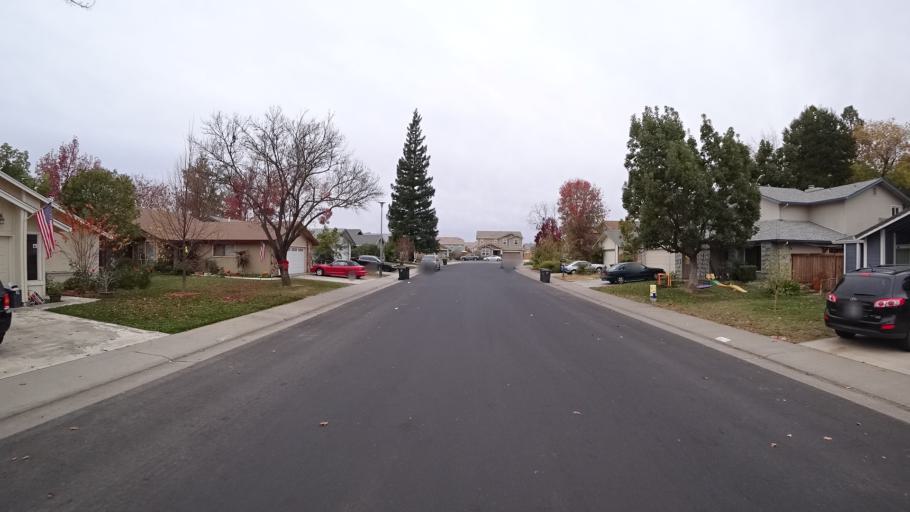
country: US
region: California
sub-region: Sacramento County
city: Citrus Heights
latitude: 38.7065
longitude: -121.3010
